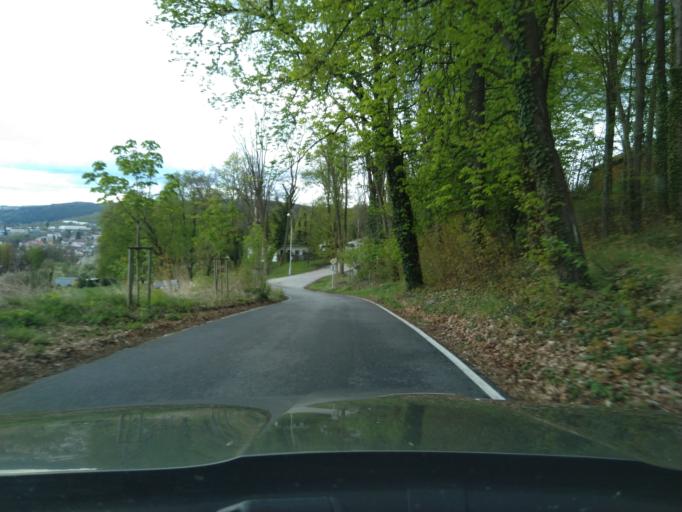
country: CZ
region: Jihocesky
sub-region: Okres Prachatice
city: Vimperk
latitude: 49.0576
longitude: 13.7715
